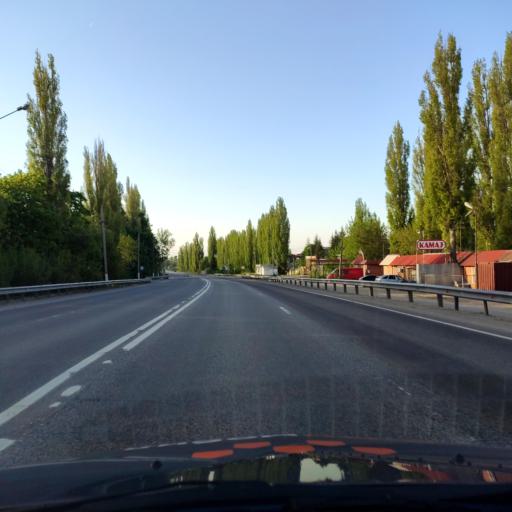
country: RU
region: Lipetsk
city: Yelets
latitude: 52.6099
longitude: 38.4634
